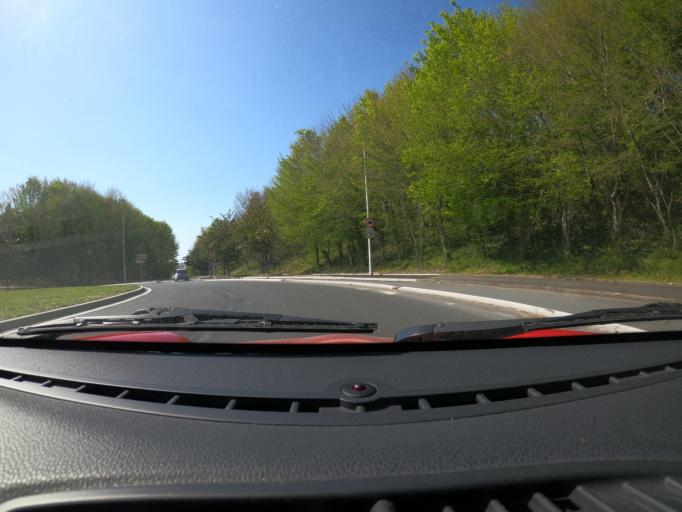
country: FR
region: Aquitaine
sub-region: Departement des Pyrenees-Atlantiques
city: Bayonne
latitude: 43.5024
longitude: -1.4785
